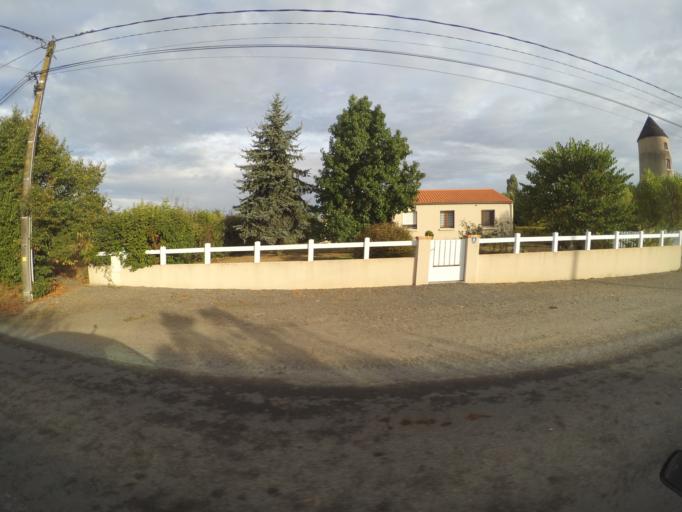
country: FR
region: Pays de la Loire
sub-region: Departement de la Loire-Atlantique
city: La Planche
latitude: 47.0042
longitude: -1.4607
